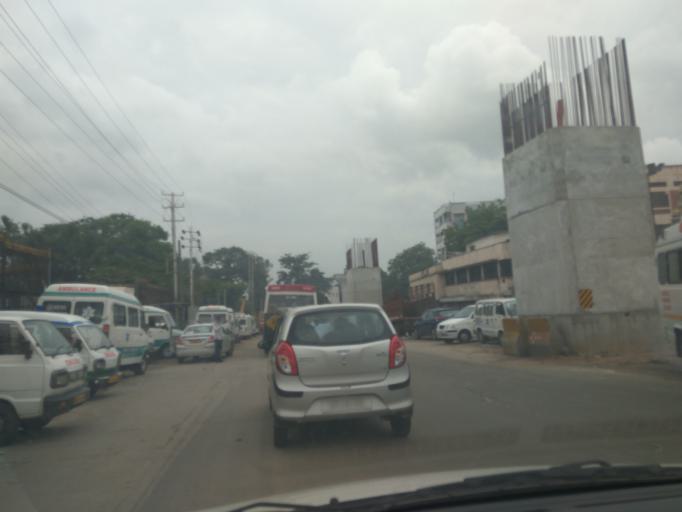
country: IN
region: Telangana
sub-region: Hyderabad
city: Malkajgiri
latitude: 17.4231
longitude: 78.5018
